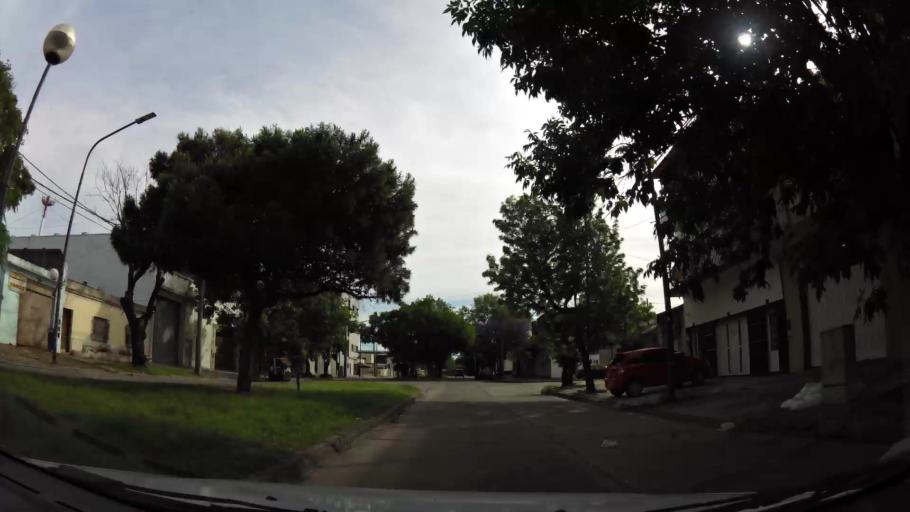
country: AR
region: Buenos Aires F.D.
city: Villa Lugano
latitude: -34.6571
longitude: -58.4948
